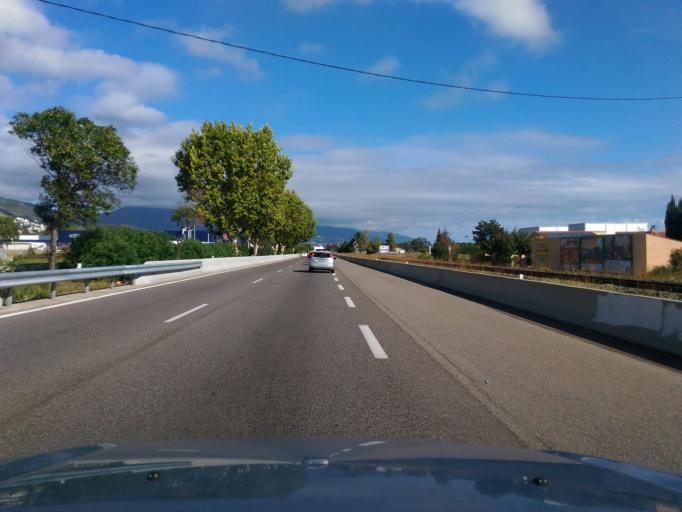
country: FR
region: Corsica
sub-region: Departement de la Haute-Corse
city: Biguglia
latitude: 42.6032
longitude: 9.4384
